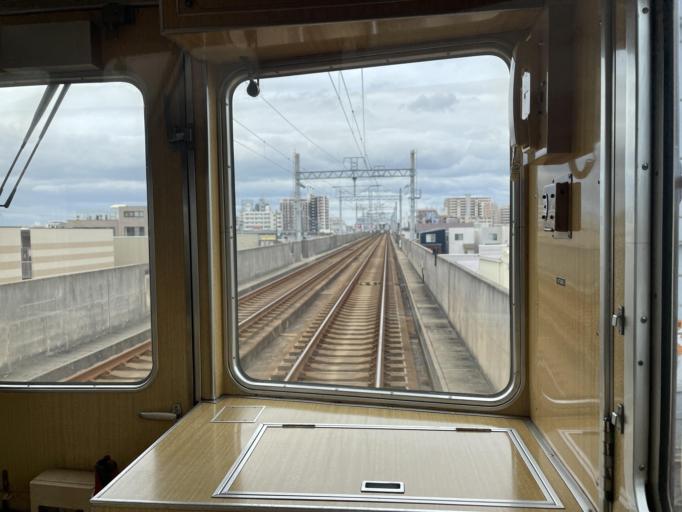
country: JP
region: Hyogo
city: Nishinomiya-hama
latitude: 34.7357
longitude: 135.3538
